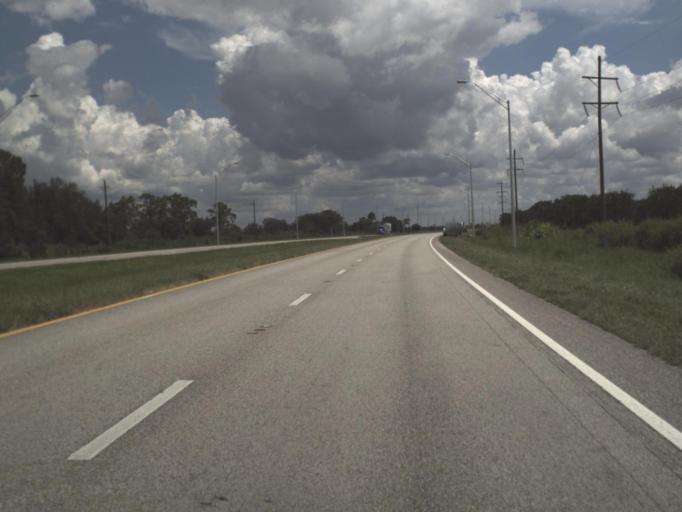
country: US
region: Florida
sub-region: Polk County
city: Babson Park
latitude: 27.8685
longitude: -81.3860
